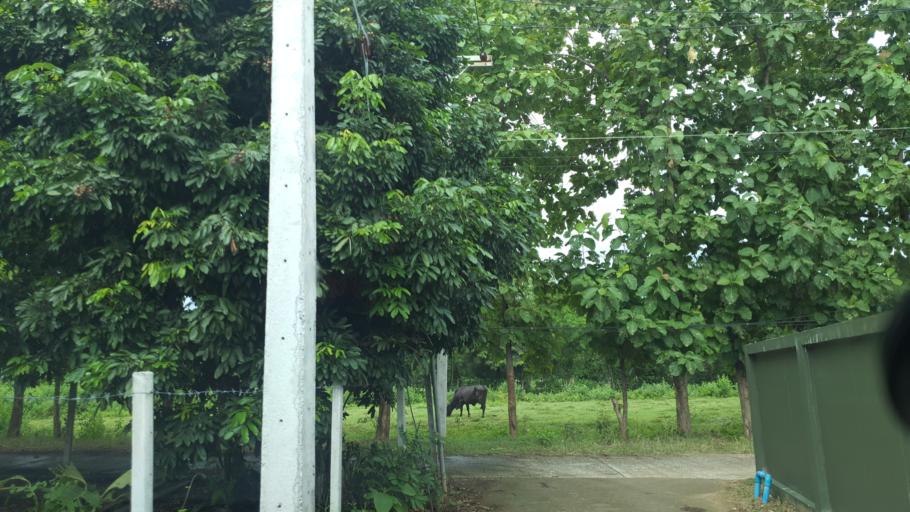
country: TH
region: Chiang Mai
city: Mae On
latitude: 18.7478
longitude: 99.2292
